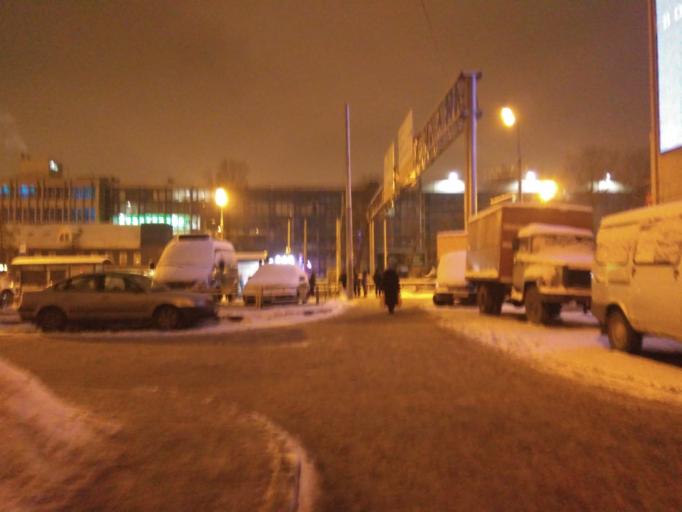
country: RU
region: Moscow
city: Lefortovo
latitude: 55.7482
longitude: 37.7028
